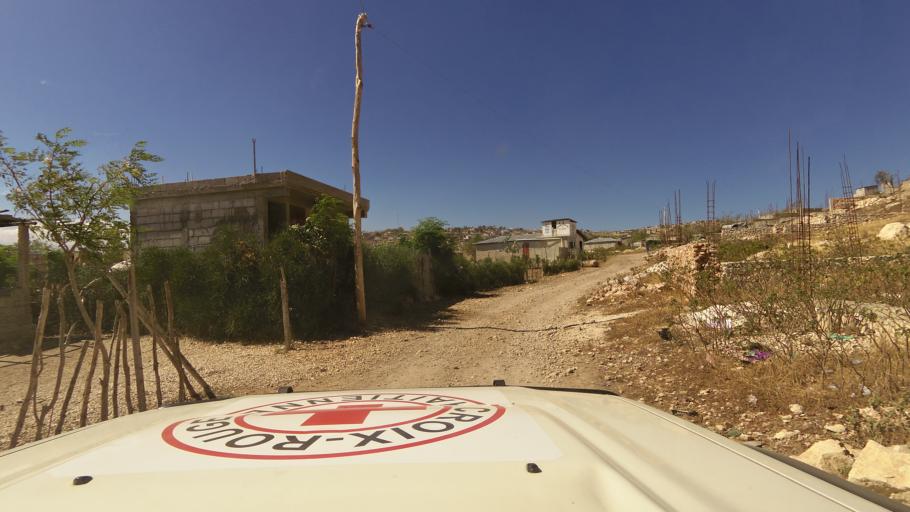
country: HT
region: Ouest
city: Croix des Bouquets
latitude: 18.6624
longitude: -72.2630
